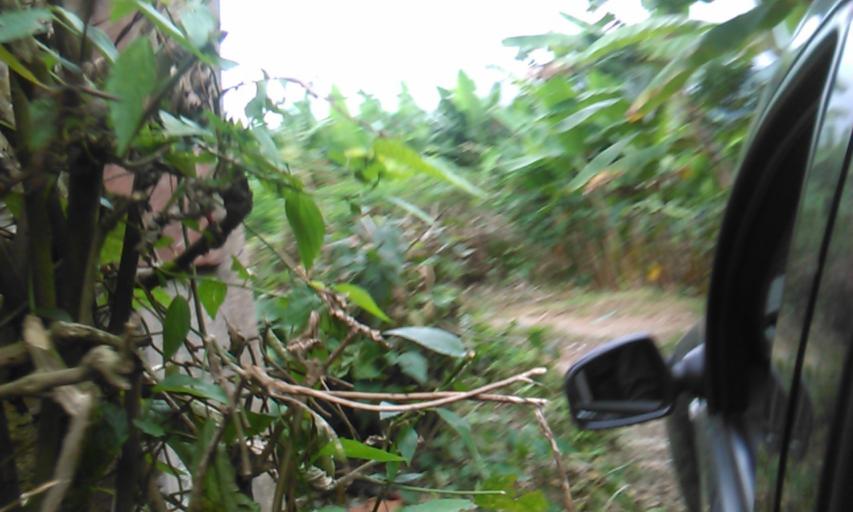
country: CO
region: Quindio
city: Cordoba
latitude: 4.4091
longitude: -75.6835
